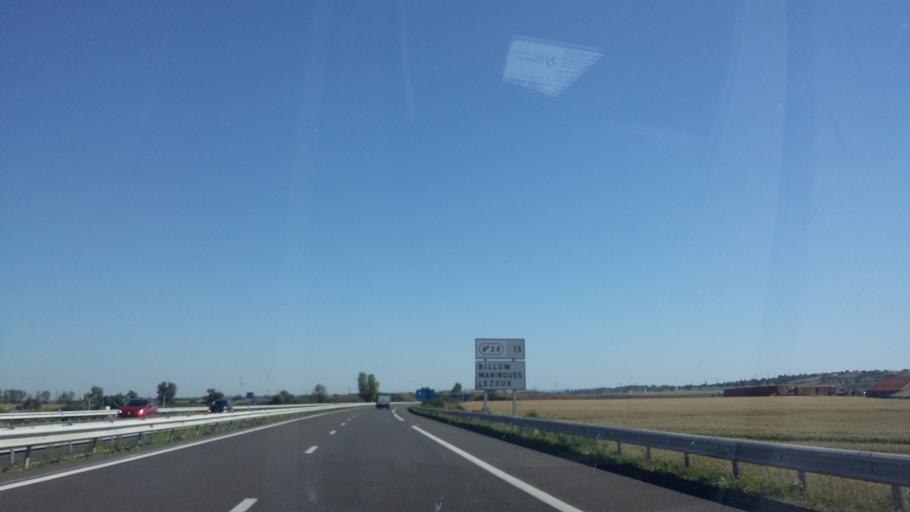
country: FR
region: Auvergne
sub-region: Departement du Puy-de-Dome
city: Malintrat
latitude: 45.7927
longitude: 3.2040
